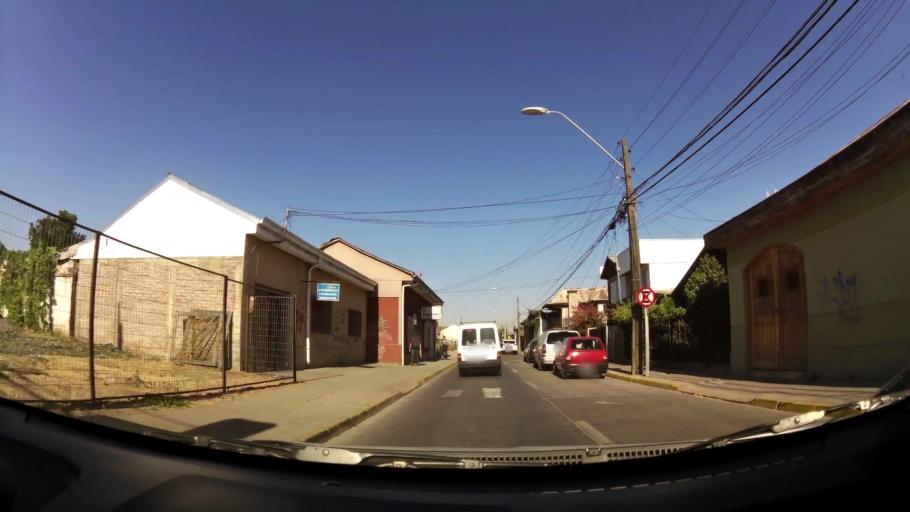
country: CL
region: Maule
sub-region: Provincia de Curico
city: Curico
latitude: -34.9873
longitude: -71.2427
